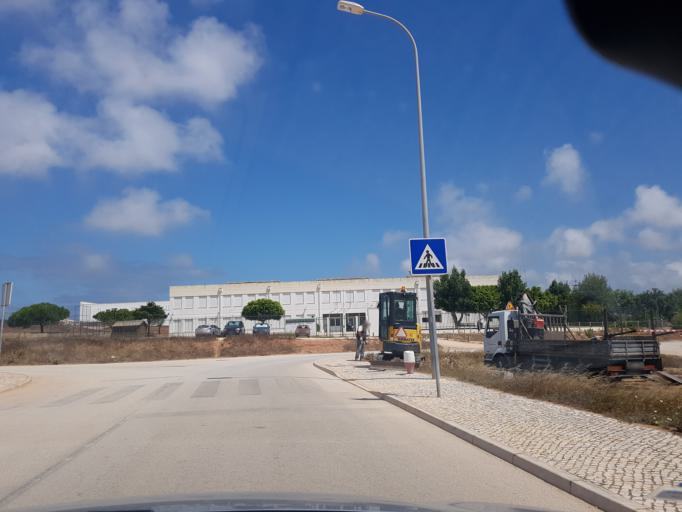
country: PT
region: Faro
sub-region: Vila do Bispo
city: Vila do Bispo
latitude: 37.0813
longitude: -8.9139
